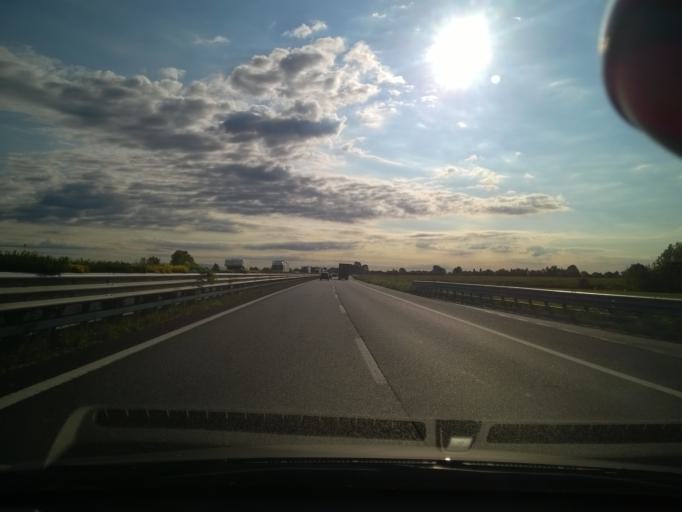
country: IT
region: Veneto
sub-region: Provincia di Venezia
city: Teglio Veneto
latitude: 45.8050
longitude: 12.8958
